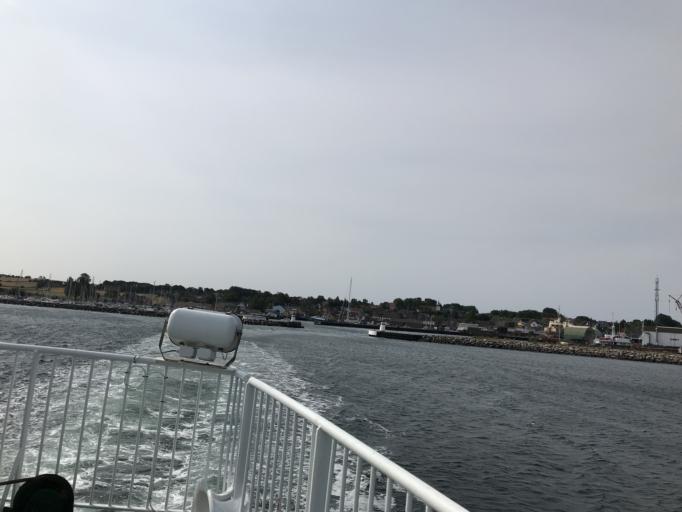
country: DK
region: South Denmark
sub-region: Faaborg-Midtfyn Kommune
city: Faaborg
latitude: 54.9455
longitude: 10.2584
